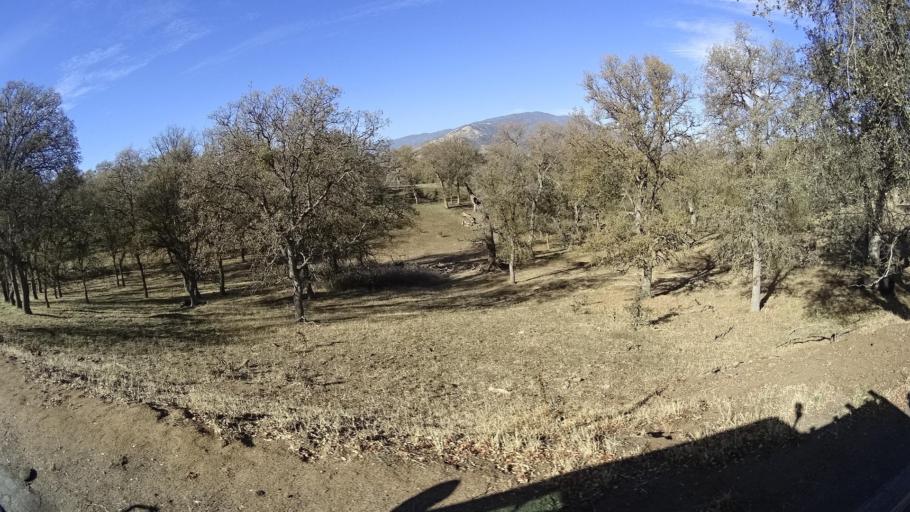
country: US
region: California
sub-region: Kern County
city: Bear Valley Springs
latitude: 35.3572
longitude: -118.5584
